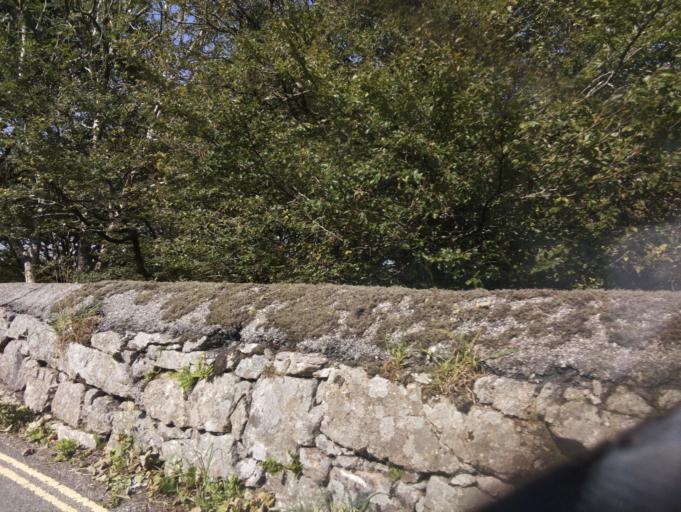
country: GB
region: England
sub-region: Devon
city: Yelverton
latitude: 50.5542
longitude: -4.0028
